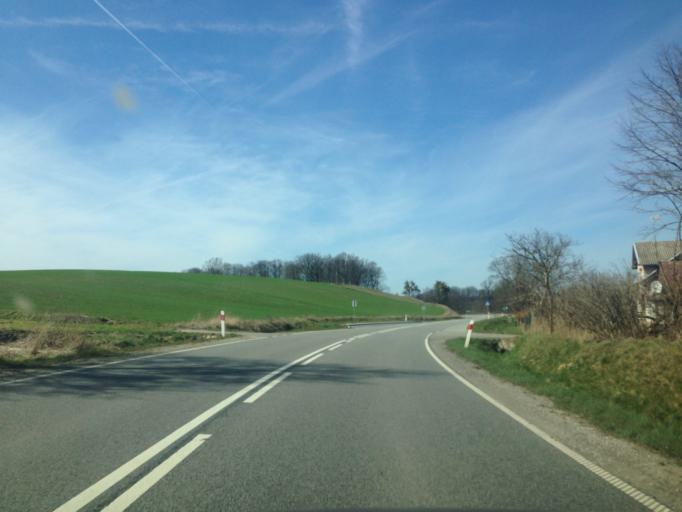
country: PL
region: Pomeranian Voivodeship
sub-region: Powiat starogardzki
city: Smetowo Graniczne
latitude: 53.7361
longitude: 18.7133
